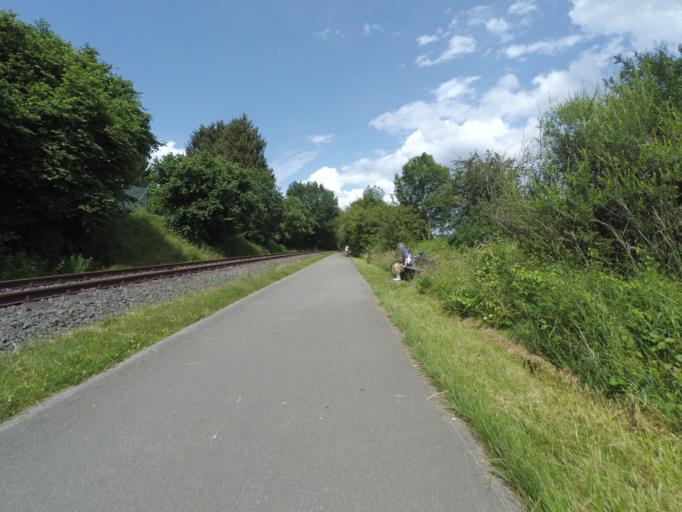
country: DE
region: North Rhine-Westphalia
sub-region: Regierungsbezirk Koln
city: Roetgen
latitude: 50.7091
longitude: 6.1850
